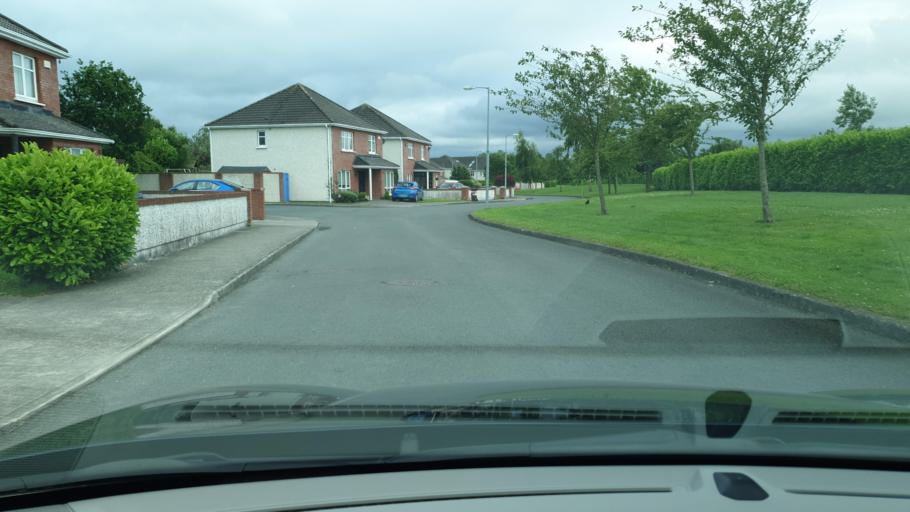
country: IE
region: Leinster
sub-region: An Mhi
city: Ratoath
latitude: 53.5060
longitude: -6.4737
